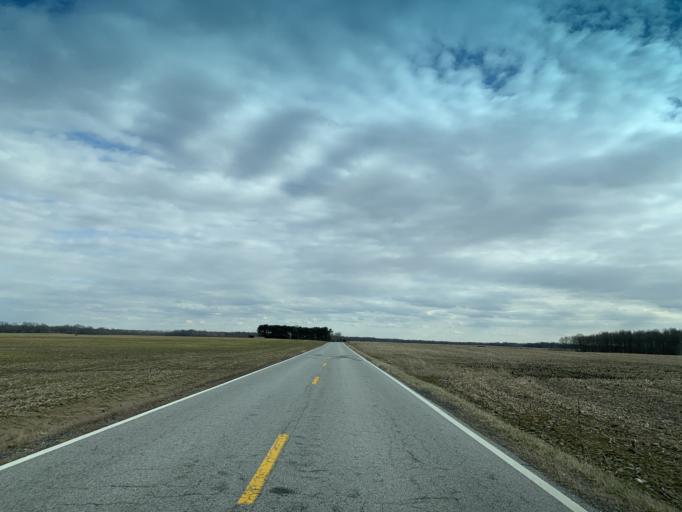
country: US
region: Maryland
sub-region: Caroline County
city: Ridgely
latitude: 38.9968
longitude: -75.9534
